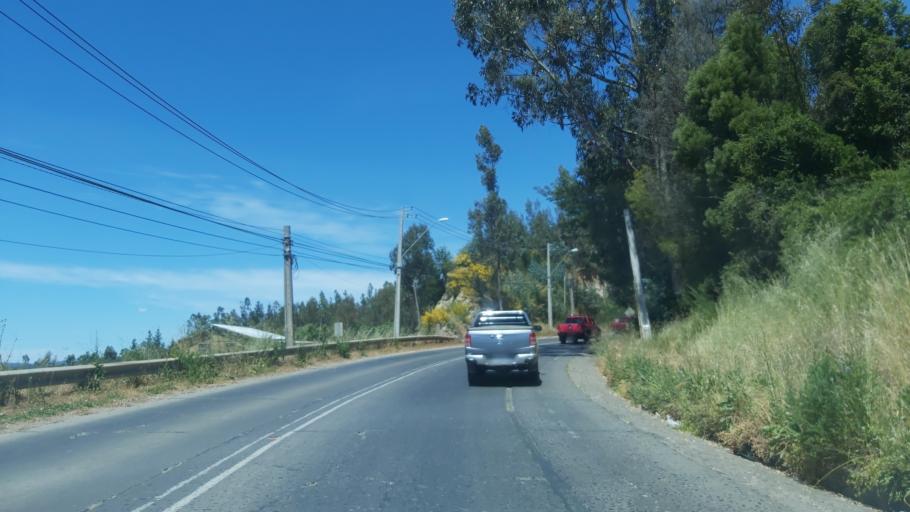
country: CL
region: Maule
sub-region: Provincia de Talca
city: Constitucion
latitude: -35.3499
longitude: -72.4091
